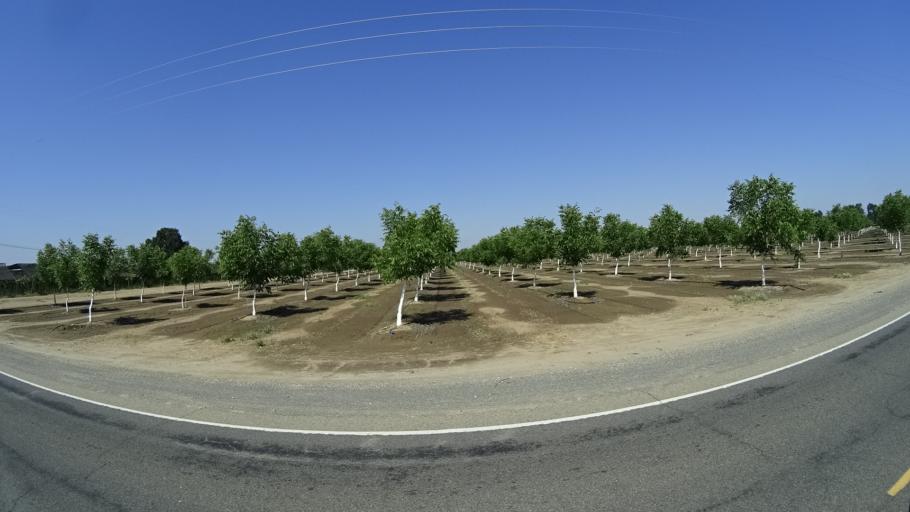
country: US
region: California
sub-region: Fresno County
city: Kingsburg
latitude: 36.4380
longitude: -119.5647
